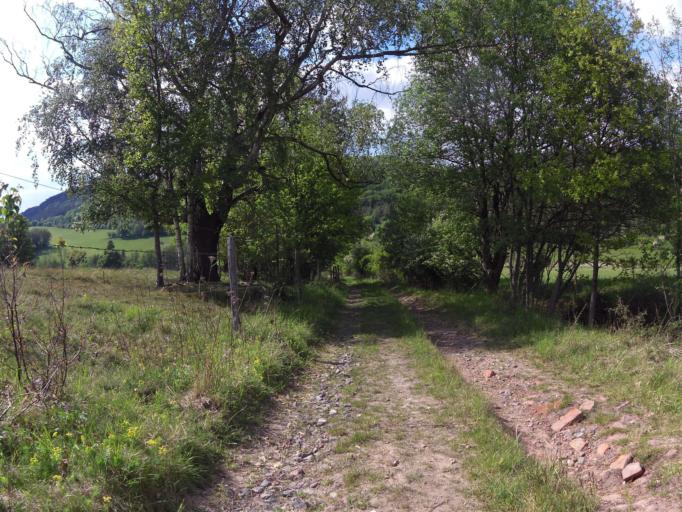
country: DE
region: Thuringia
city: Seebach
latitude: 50.9595
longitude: 10.4263
